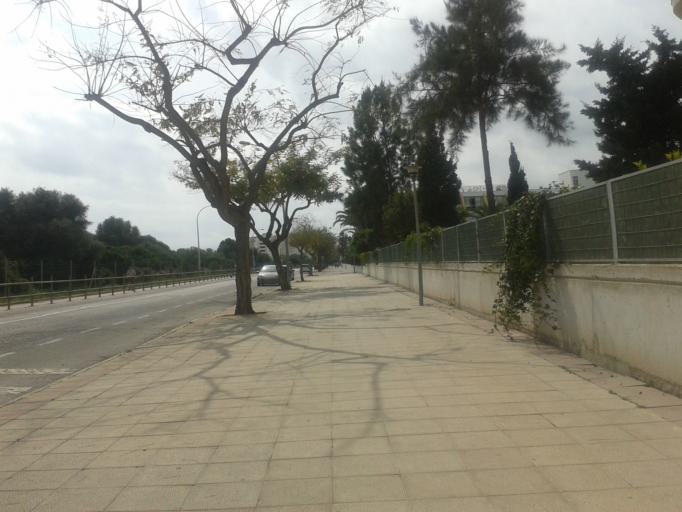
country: ES
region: Balearic Islands
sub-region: Illes Balears
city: Son Servera
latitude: 39.5812
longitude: 3.3800
